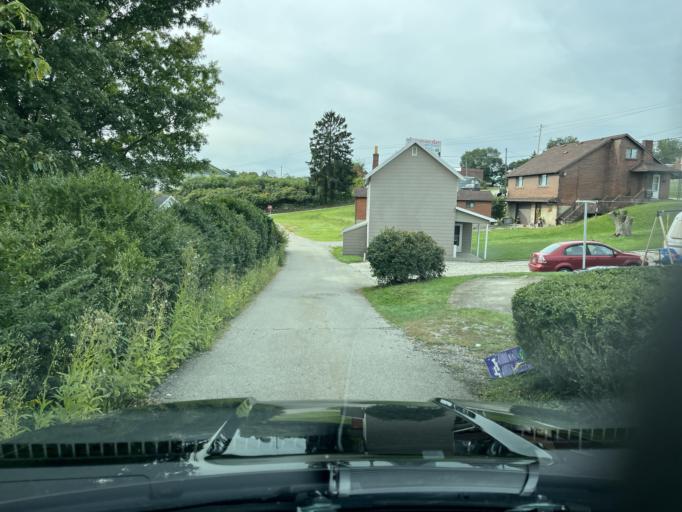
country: US
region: Pennsylvania
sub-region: Fayette County
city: Leith-Hatfield
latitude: 39.8868
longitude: -79.7363
